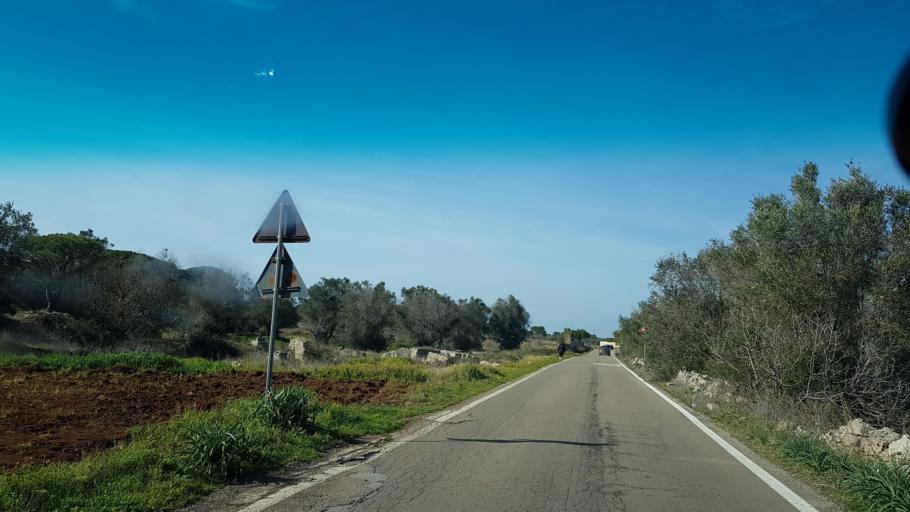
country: IT
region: Apulia
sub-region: Provincia di Lecce
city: Arnesano
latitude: 40.3513
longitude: 18.1065
